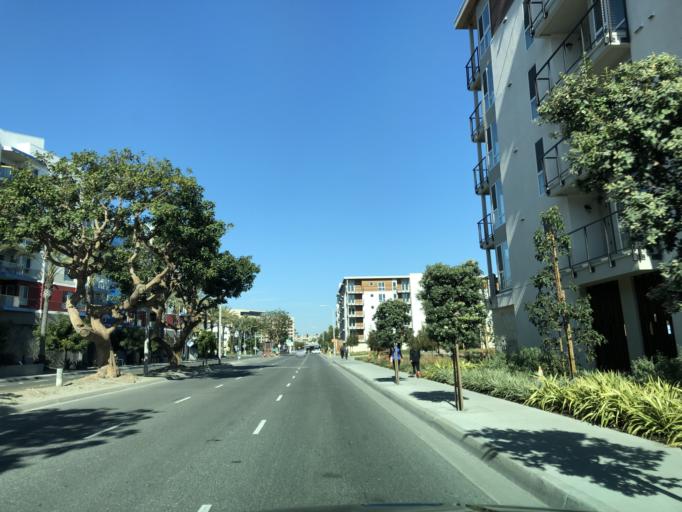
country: US
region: California
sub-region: Los Angeles County
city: Marina del Rey
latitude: 33.9771
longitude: -118.4590
